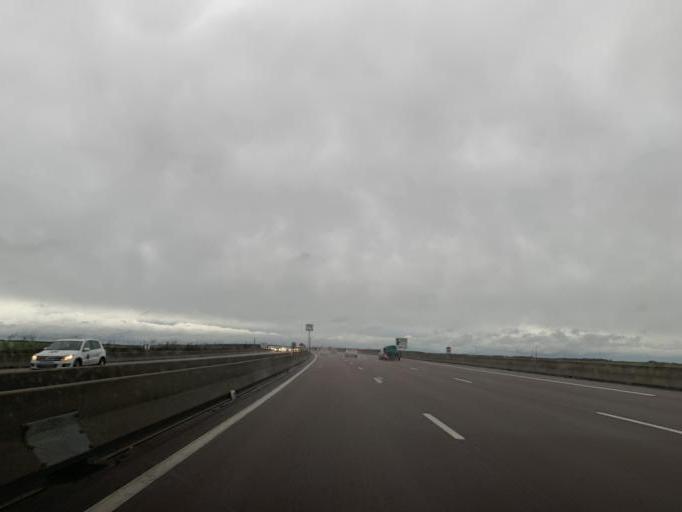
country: FR
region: Champagne-Ardenne
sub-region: Departement de la Haute-Marne
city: Langres
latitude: 47.7731
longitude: 5.2057
